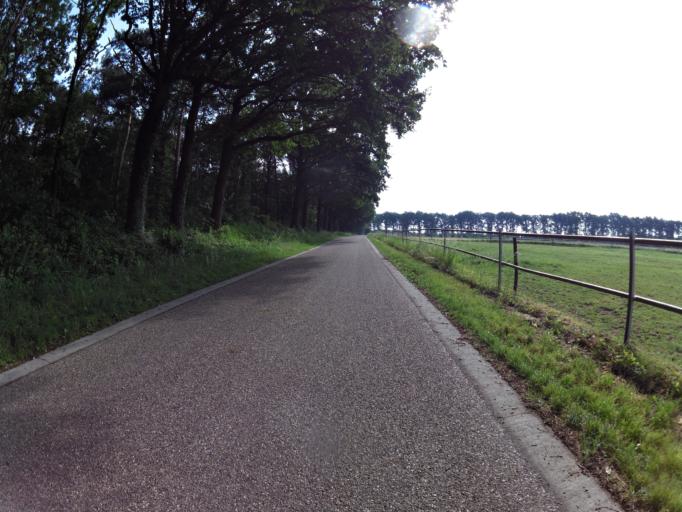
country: DE
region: North Rhine-Westphalia
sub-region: Regierungsbezirk Koln
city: Waldfeucht
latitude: 51.0837
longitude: 5.9716
